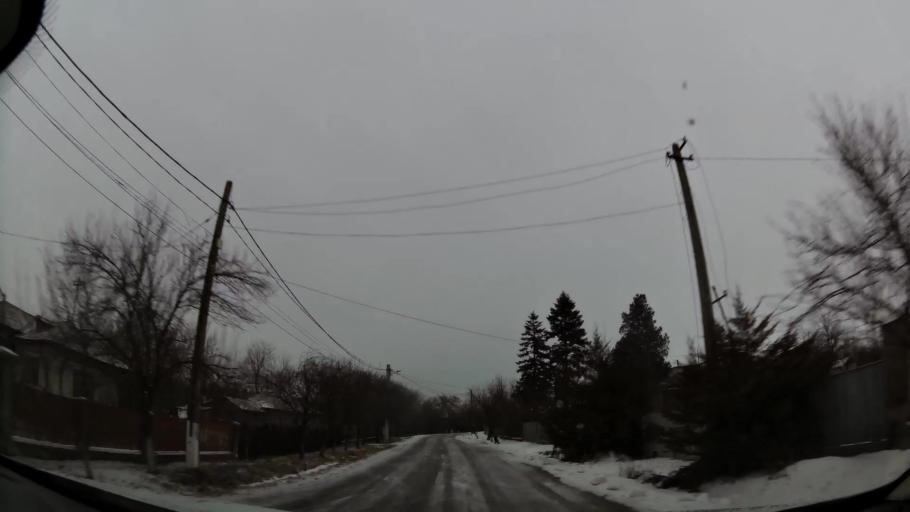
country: RO
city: Fantanele
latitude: 44.7332
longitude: 25.8952
